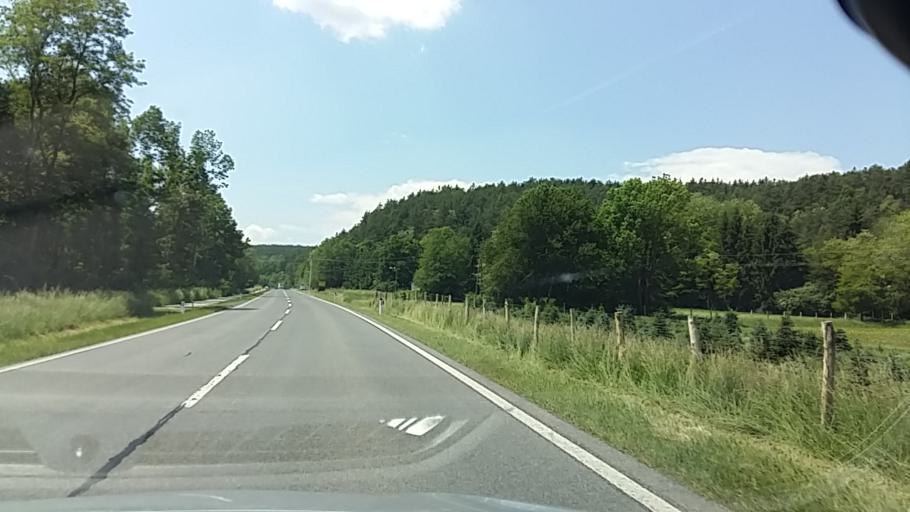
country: AT
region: Burgenland
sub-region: Politischer Bezirk Oberpullendorf
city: Oberpullendorf
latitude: 47.4846
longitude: 16.4667
